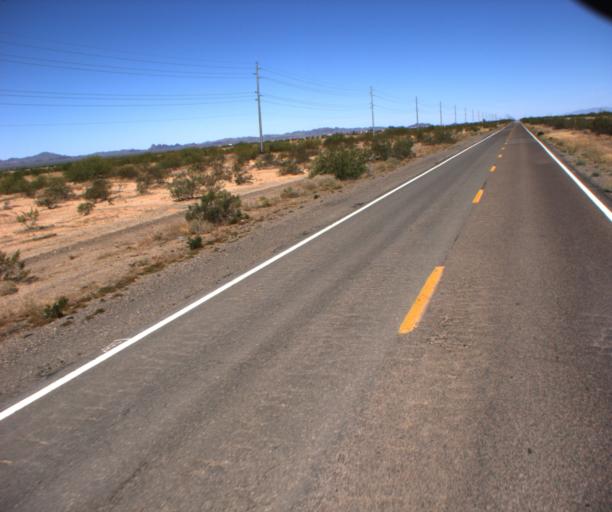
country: US
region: Arizona
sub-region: La Paz County
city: Salome
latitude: 33.8418
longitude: -113.8915
